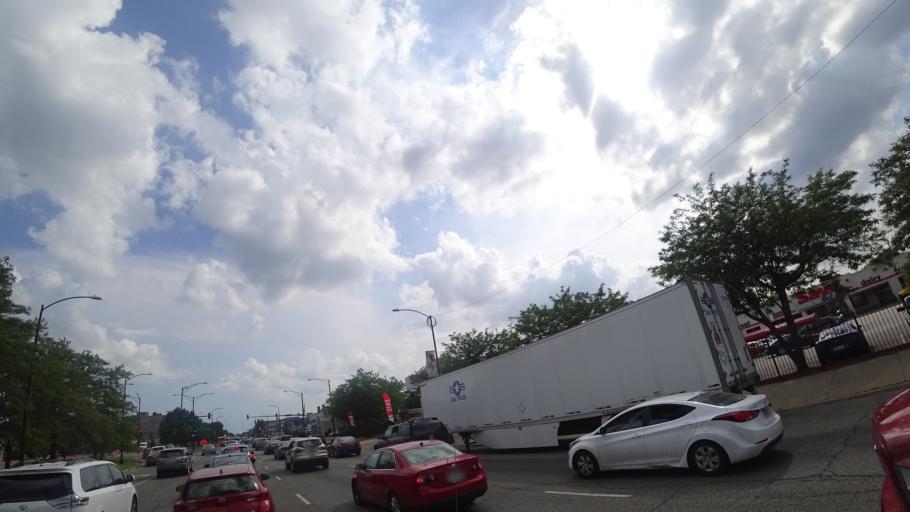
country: US
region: Illinois
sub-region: Cook County
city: Chicago
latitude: 41.7631
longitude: -87.5862
